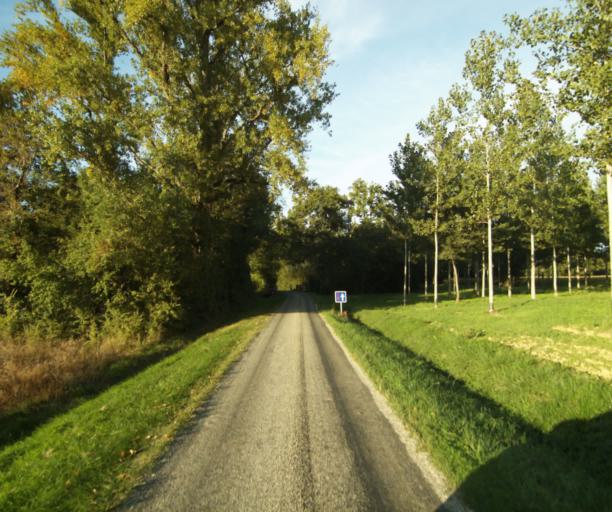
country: FR
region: Midi-Pyrenees
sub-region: Departement du Gers
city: Cazaubon
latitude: 43.8736
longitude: -0.0036
